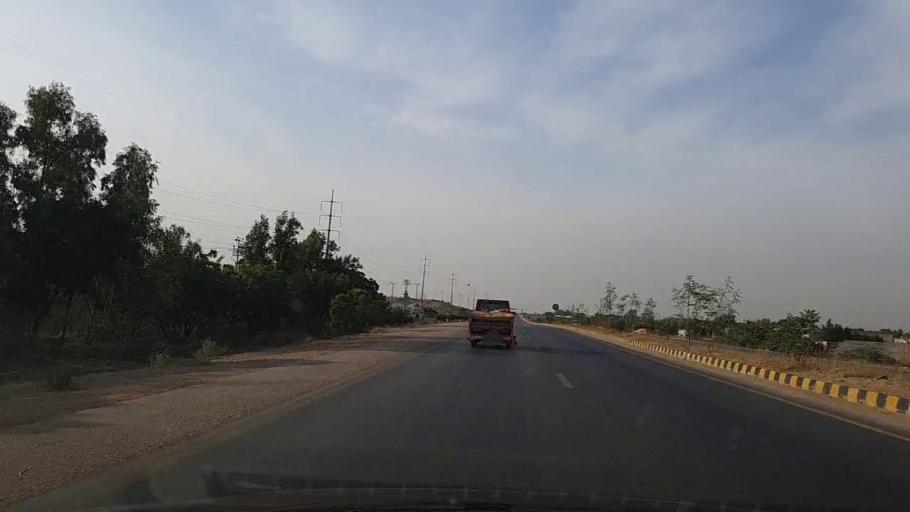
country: PK
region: Sindh
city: Gharo
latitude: 24.7582
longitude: 67.5606
